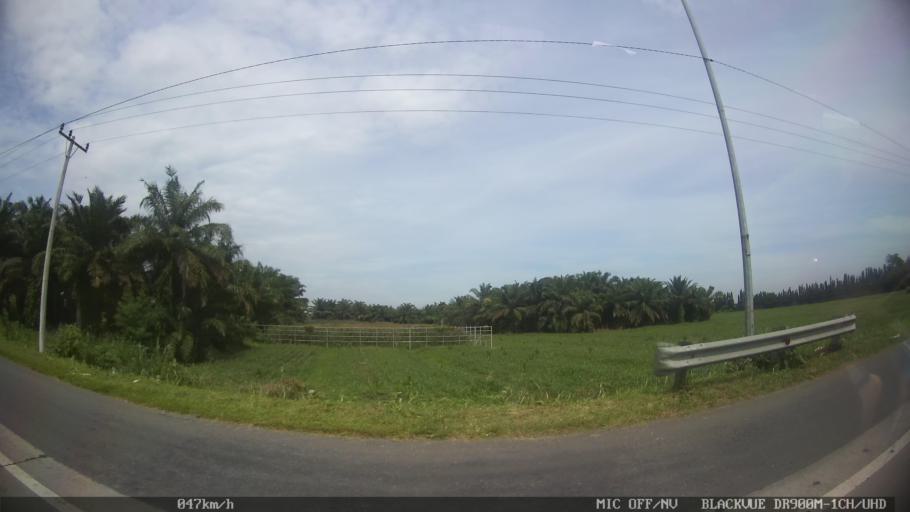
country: ID
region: North Sumatra
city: Sunggal
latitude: 3.6235
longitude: 98.6283
